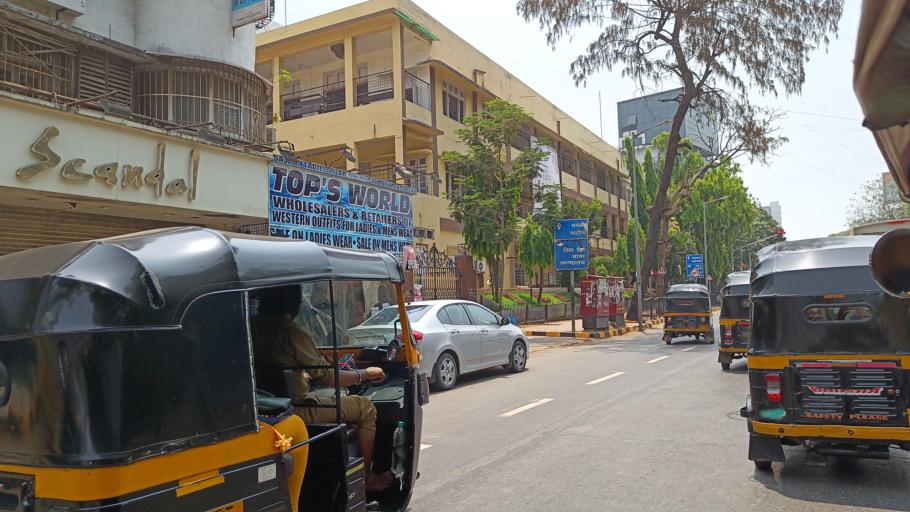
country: IN
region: Maharashtra
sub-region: Mumbai Suburban
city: Mumbai
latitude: 19.0646
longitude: 72.8348
